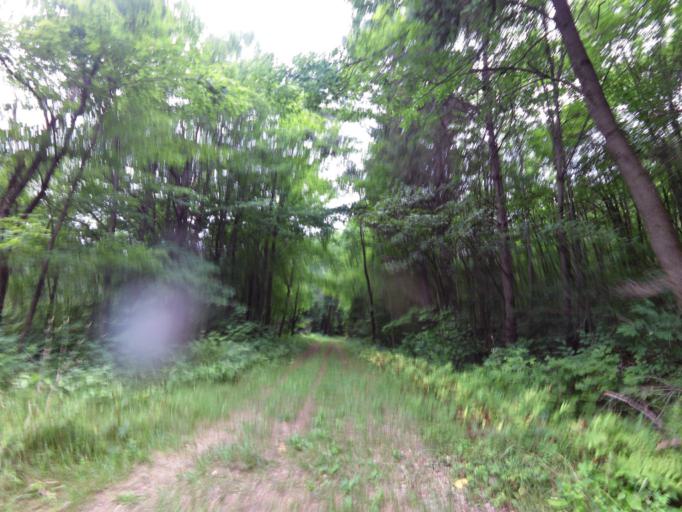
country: CA
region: Quebec
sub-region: Outaouais
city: Wakefield
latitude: 45.6163
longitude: -76.0412
